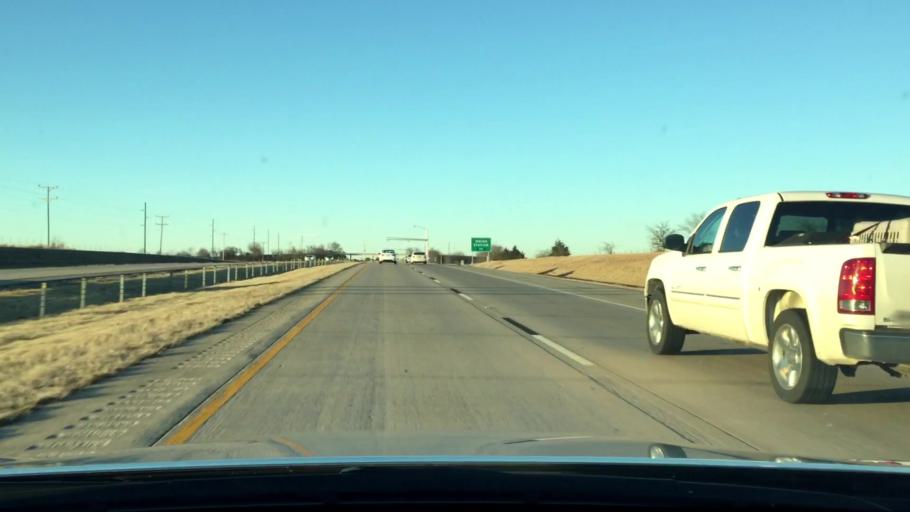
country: US
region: Oklahoma
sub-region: Love County
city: Marietta
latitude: 33.8903
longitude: -97.1344
